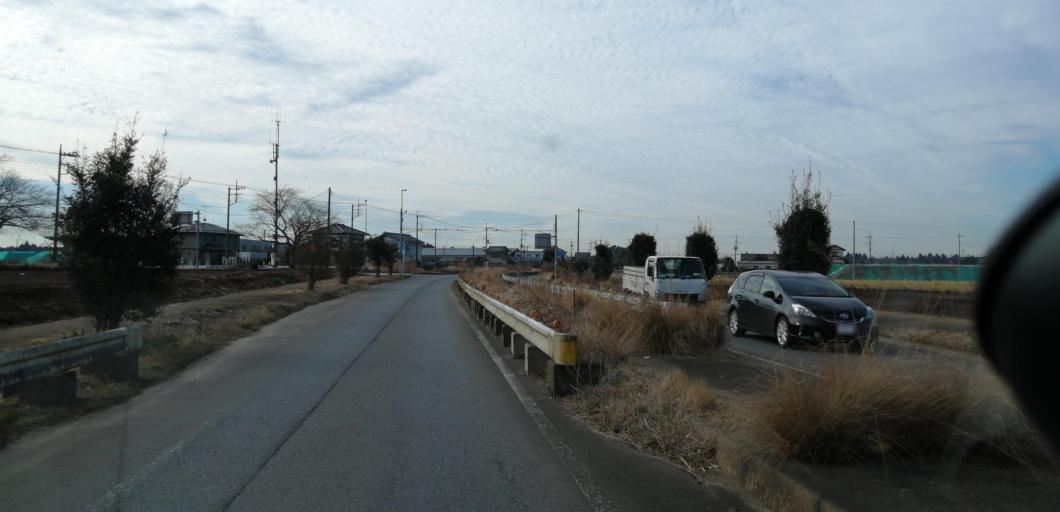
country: JP
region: Chiba
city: Narita
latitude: 35.7912
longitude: 140.4118
